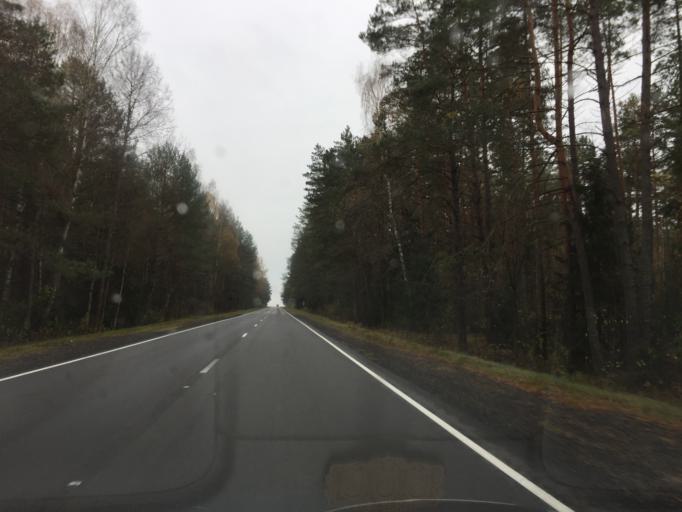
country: BY
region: Mogilev
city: Cherykaw
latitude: 53.6388
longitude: 31.2765
